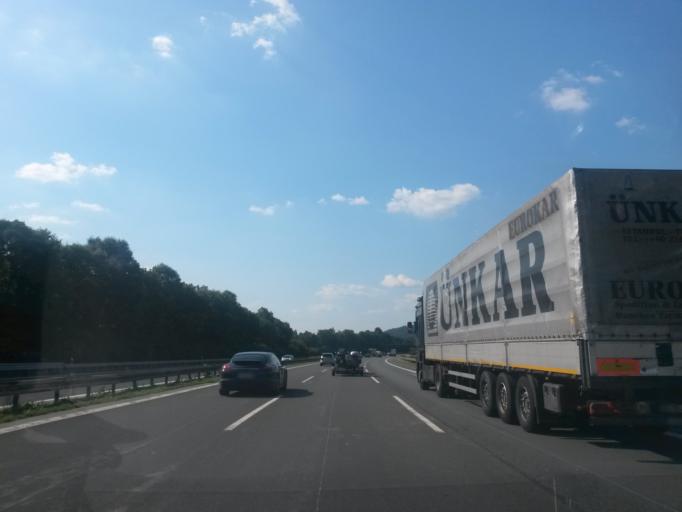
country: DE
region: Bavaria
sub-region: Regierungsbezirk Mittelfranken
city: Greding
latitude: 49.0507
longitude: 11.3317
